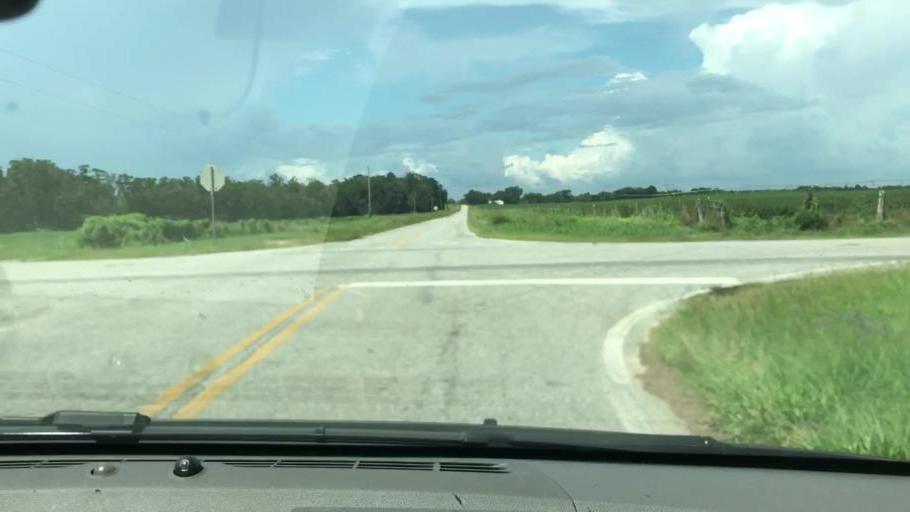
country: US
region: Georgia
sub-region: Seminole County
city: Donalsonville
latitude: 31.1816
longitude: -85.0045
